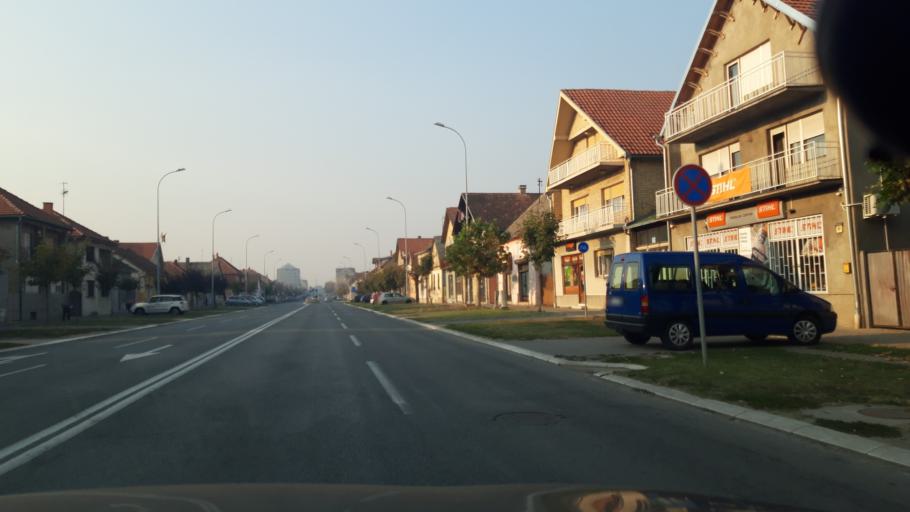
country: RS
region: Autonomna Pokrajina Vojvodina
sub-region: Sremski Okrug
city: Ingija
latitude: 45.0426
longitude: 20.0863
